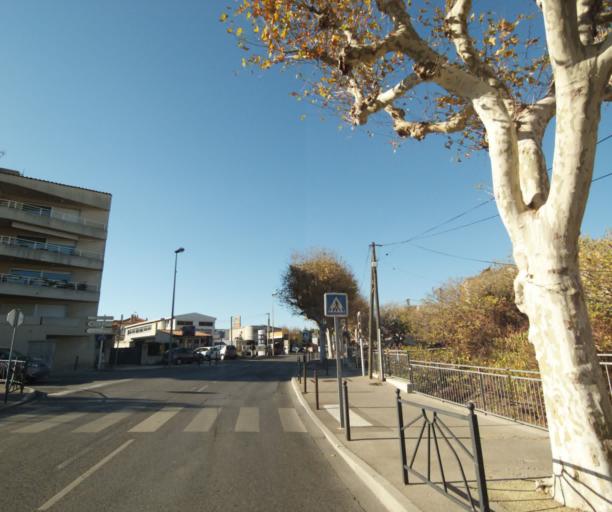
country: FR
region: Provence-Alpes-Cote d'Azur
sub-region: Departement des Bouches-du-Rhone
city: La Ciotat
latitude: 43.1836
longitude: 5.6105
